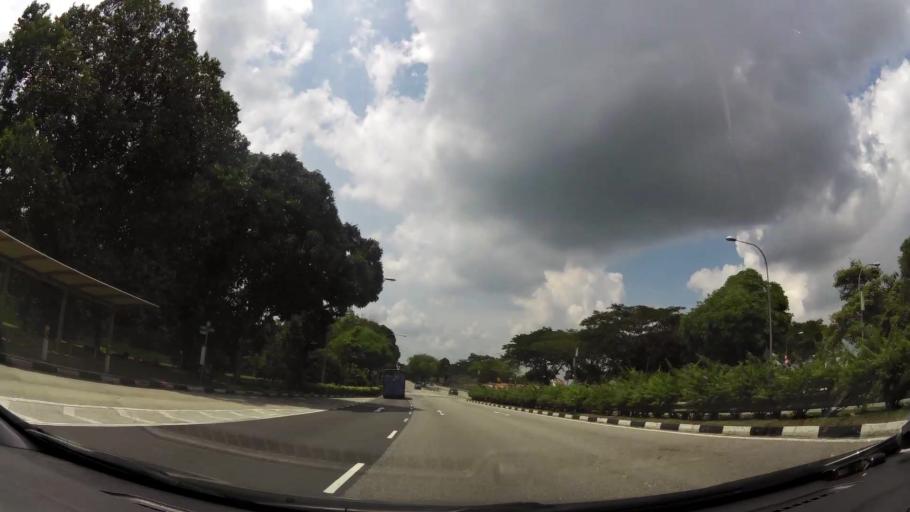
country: MY
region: Johor
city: Johor Bahru
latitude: 1.4161
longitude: 103.8020
